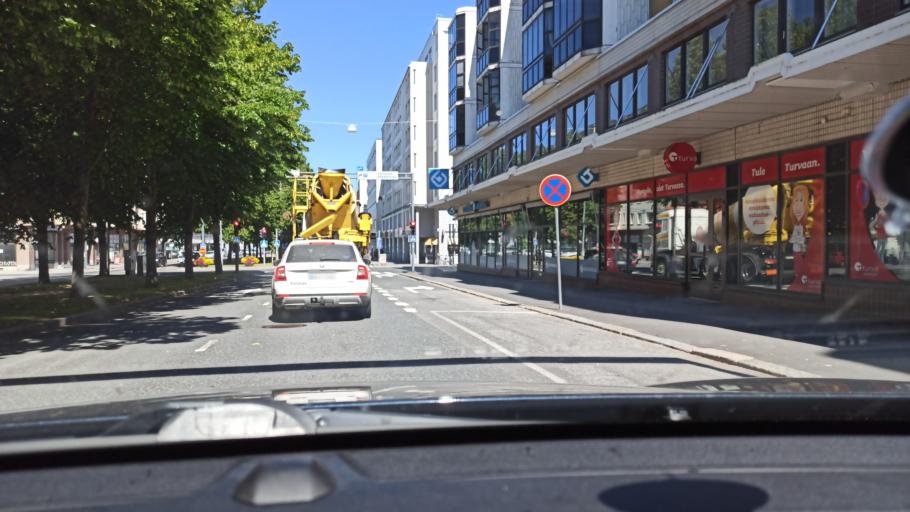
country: FI
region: Ostrobothnia
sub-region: Vaasa
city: Vaasa
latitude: 63.0932
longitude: 21.6185
